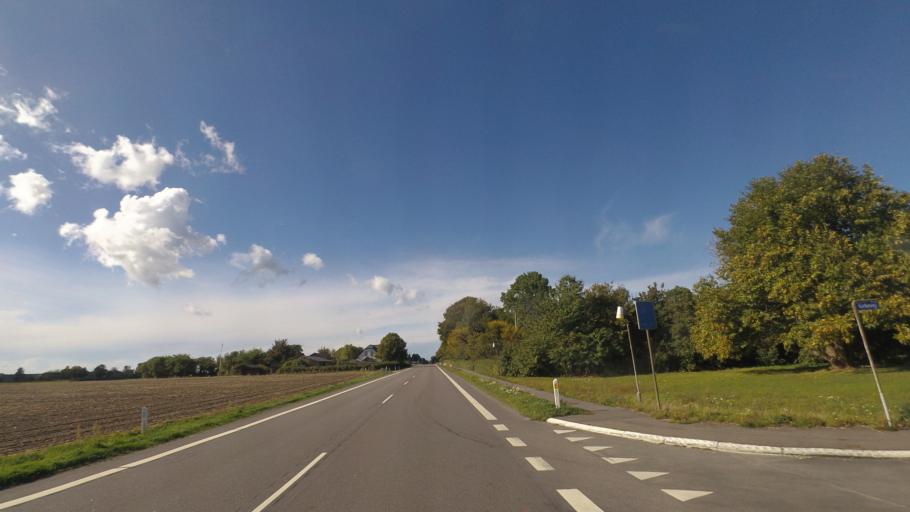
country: DK
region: Capital Region
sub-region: Bornholm Kommune
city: Akirkeby
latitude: 55.0708
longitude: 14.8122
